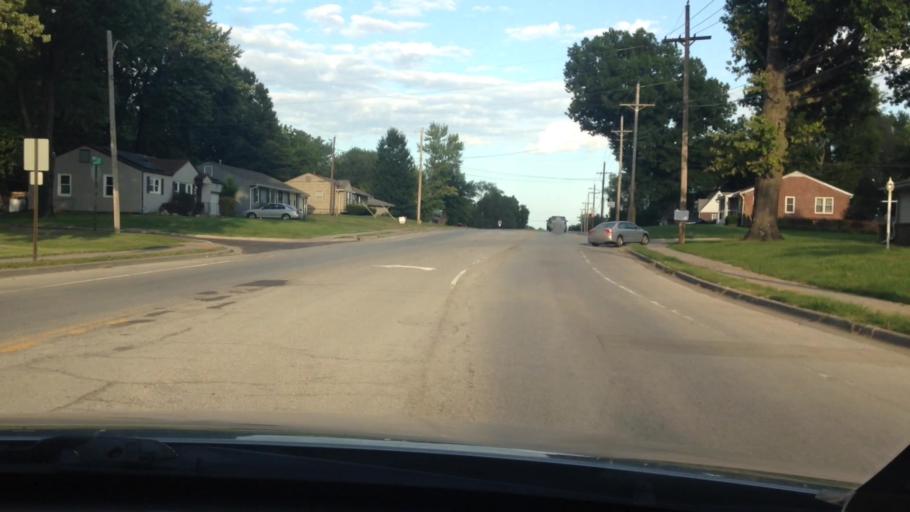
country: US
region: Missouri
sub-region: Jackson County
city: Raytown
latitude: 38.9661
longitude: -94.4888
